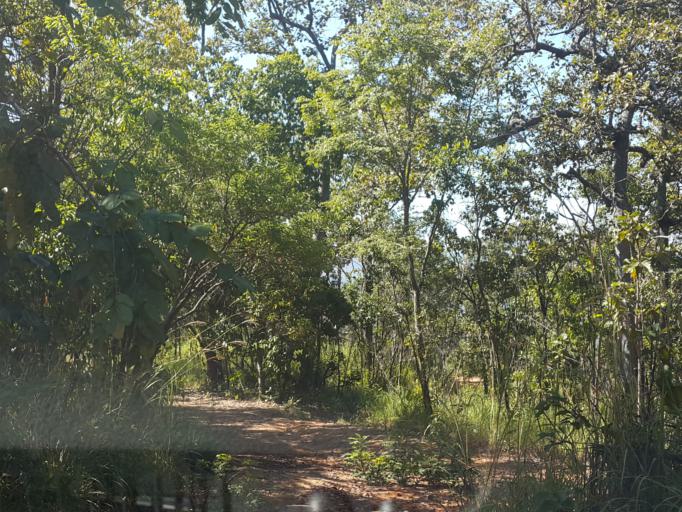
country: TH
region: Chiang Mai
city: Chiang Mai
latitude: 18.7982
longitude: 98.8659
